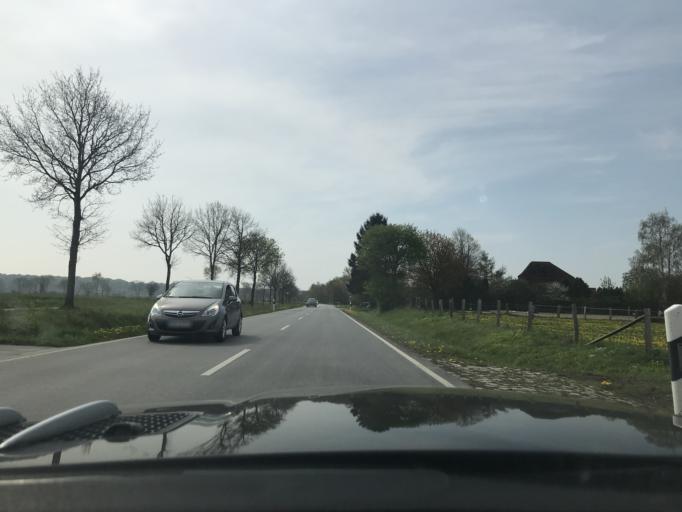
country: DE
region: Schleswig-Holstein
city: Grube
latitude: 54.2182
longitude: 11.0347
